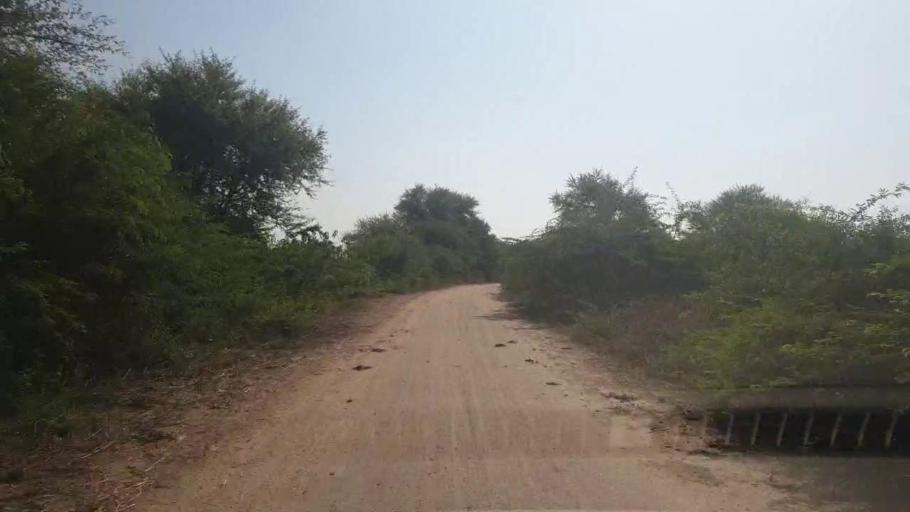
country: PK
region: Sindh
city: Badin
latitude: 24.5495
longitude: 68.8120
